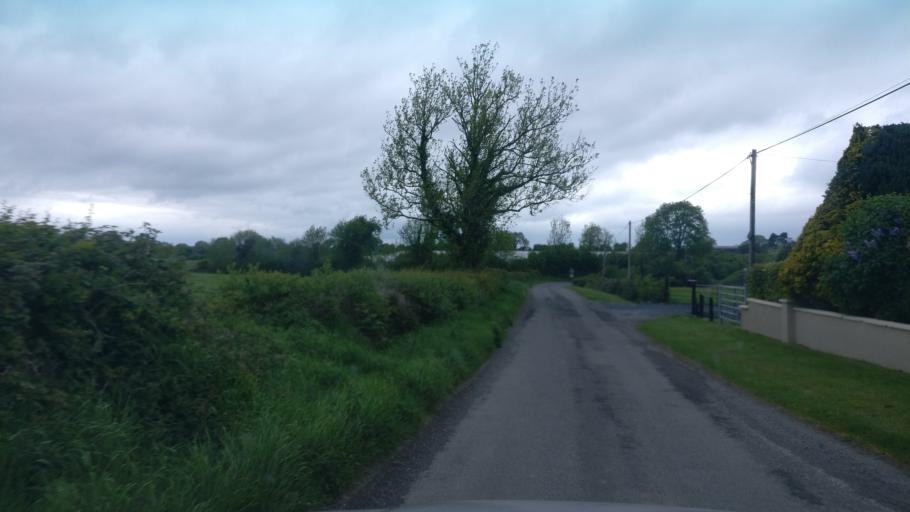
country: IE
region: Connaught
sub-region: County Galway
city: Portumna
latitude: 53.1329
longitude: -8.2917
